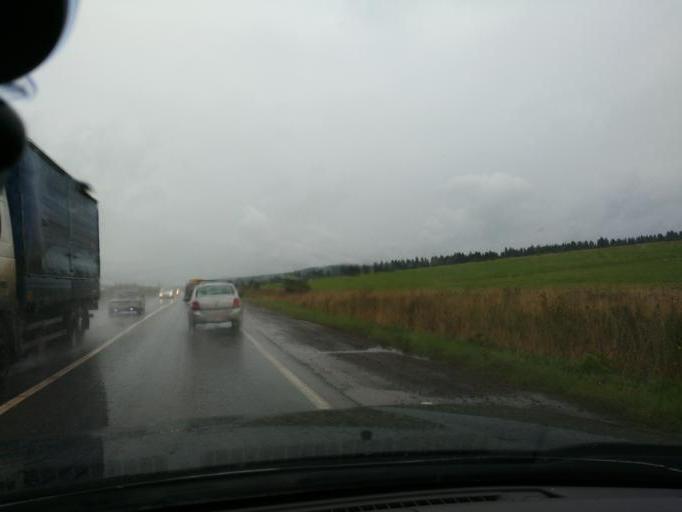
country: RU
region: Perm
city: Yugo-Kamskiy
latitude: 57.6928
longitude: 55.5878
